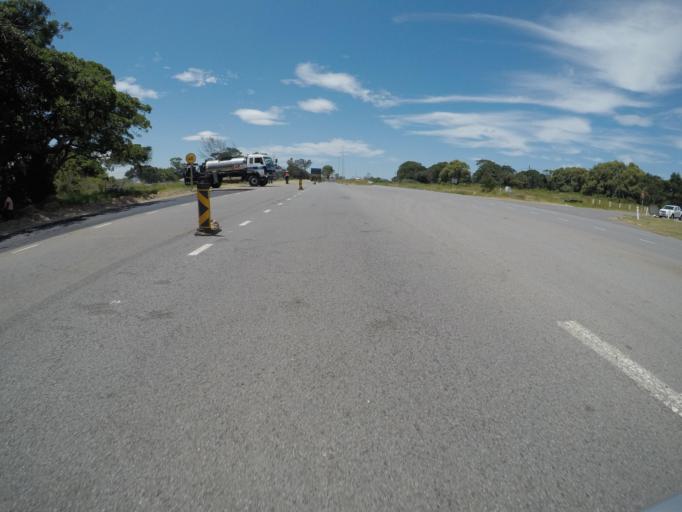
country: ZA
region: Eastern Cape
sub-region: Buffalo City Metropolitan Municipality
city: East London
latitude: -33.0353
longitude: 27.8406
